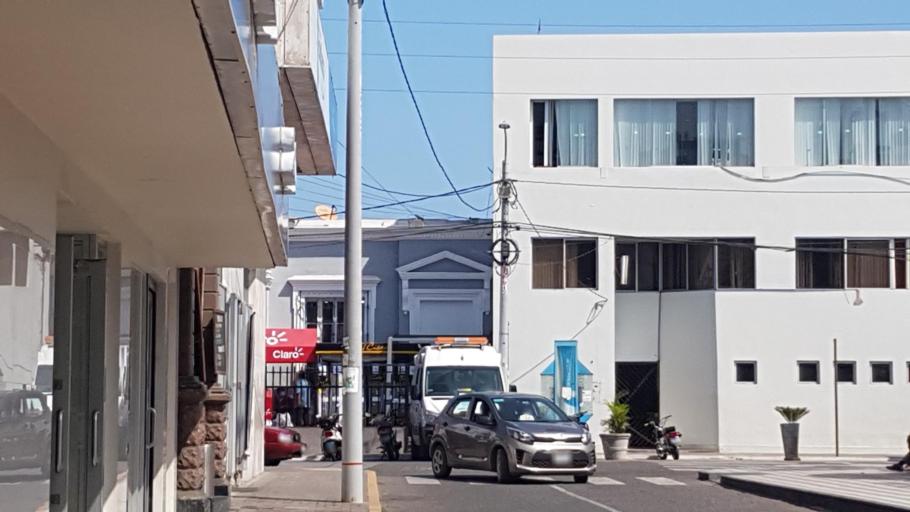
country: PE
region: Arequipa
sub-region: Provincia de Islay
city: Mollendo
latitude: -17.0294
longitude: -72.0150
